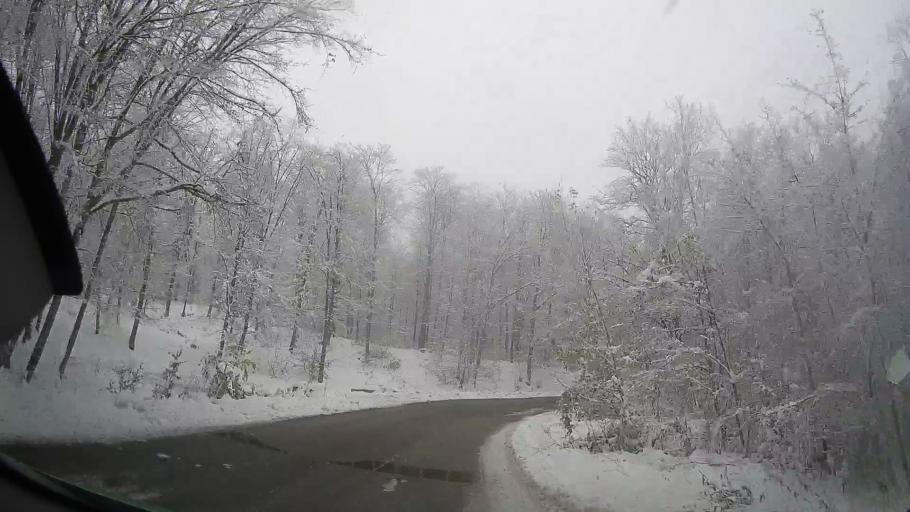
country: RO
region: Neamt
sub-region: Comuna Valea Ursului
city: Valea Ursului
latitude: 46.8459
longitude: 27.0660
